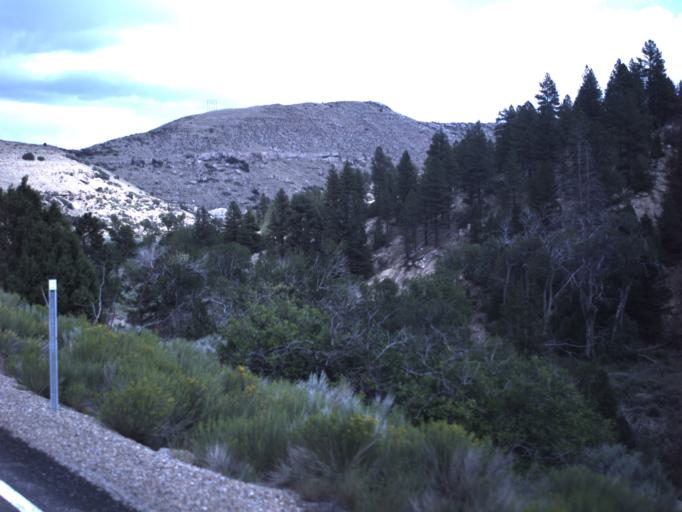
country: US
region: Utah
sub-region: Carbon County
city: Helper
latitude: 39.7737
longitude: -110.8012
